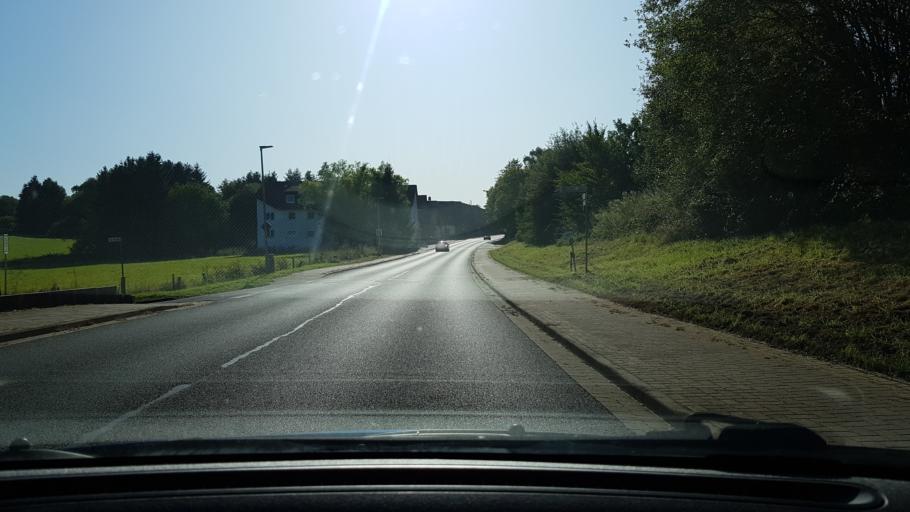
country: DE
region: Lower Saxony
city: Bad Munder am Deister
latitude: 52.2320
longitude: 9.4273
